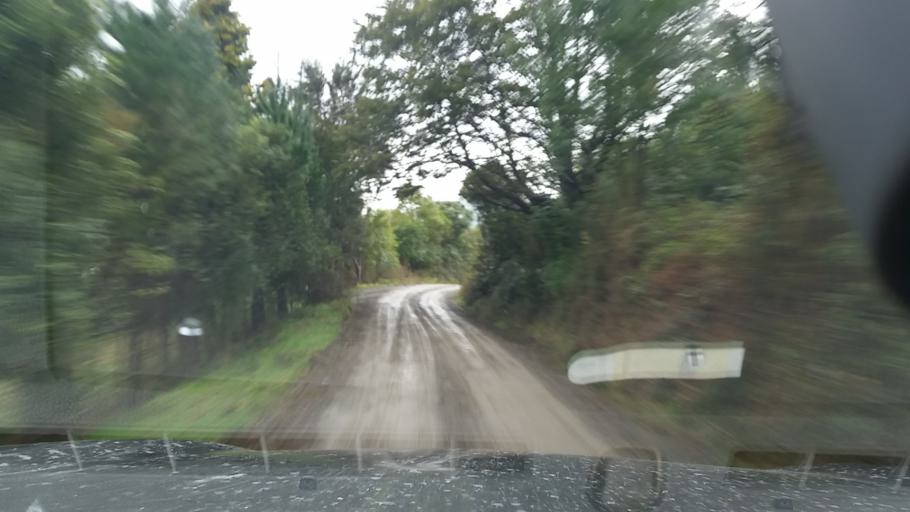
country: NZ
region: Nelson
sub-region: Nelson City
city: Nelson
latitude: -41.3606
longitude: 173.6156
